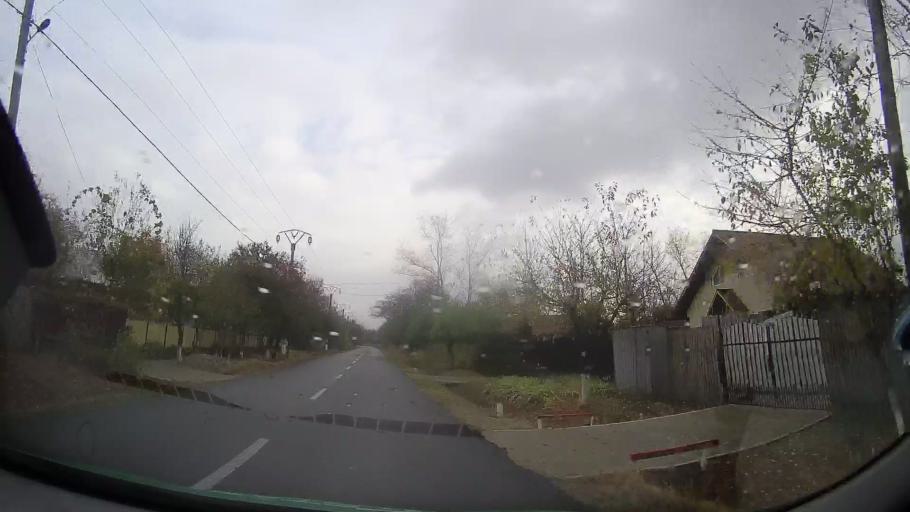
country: RO
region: Ialomita
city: Brazii
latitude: 44.7805
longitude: 26.3272
